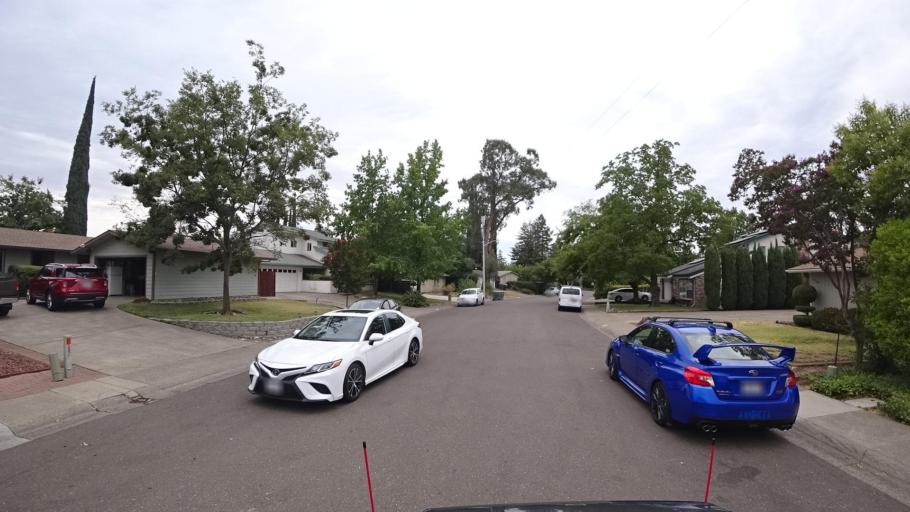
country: US
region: California
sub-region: Placer County
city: Rocklin
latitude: 38.7875
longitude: -121.2583
